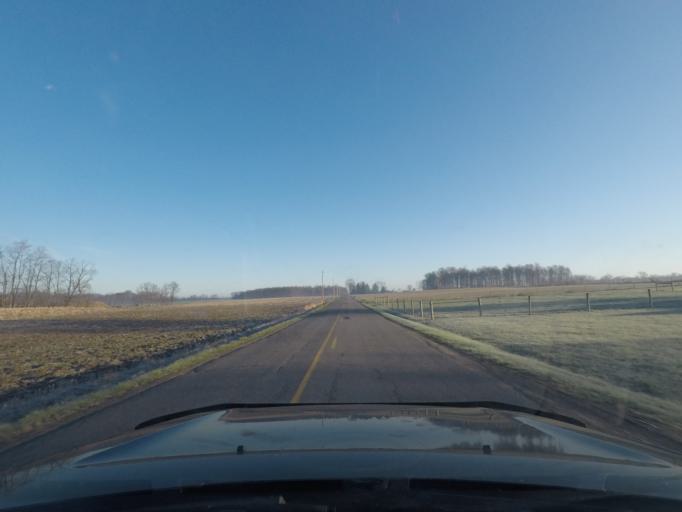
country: US
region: Indiana
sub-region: Elkhart County
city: Dunlap
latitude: 41.5658
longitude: -85.9249
